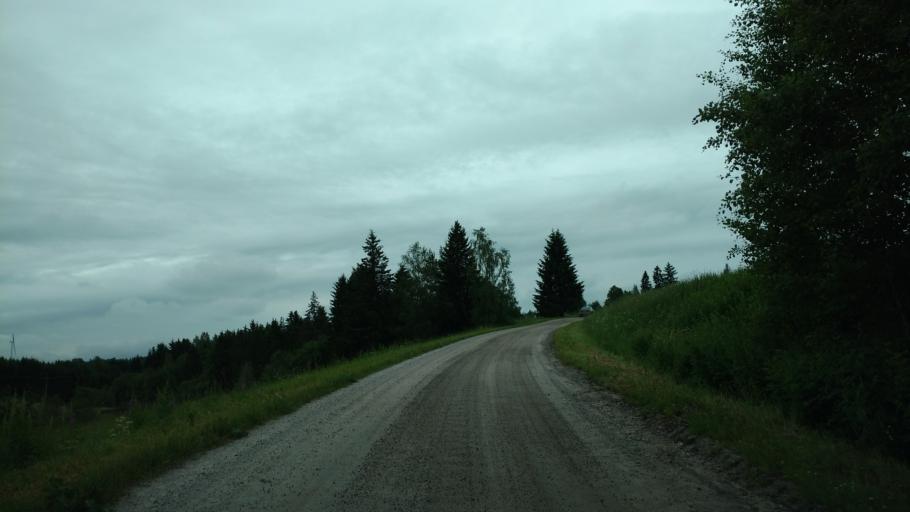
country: FI
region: Varsinais-Suomi
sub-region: Salo
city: Halikko
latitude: 60.4761
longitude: 23.0029
